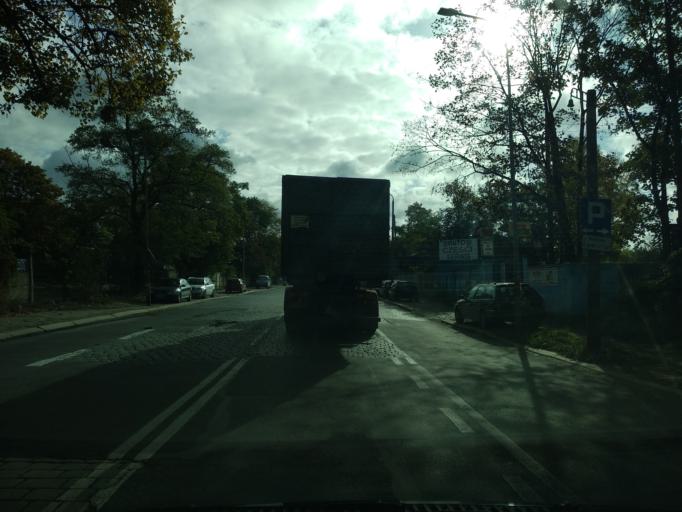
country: PL
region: Lower Silesian Voivodeship
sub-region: Powiat wroclawski
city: Wroclaw
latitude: 51.1089
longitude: 17.0097
